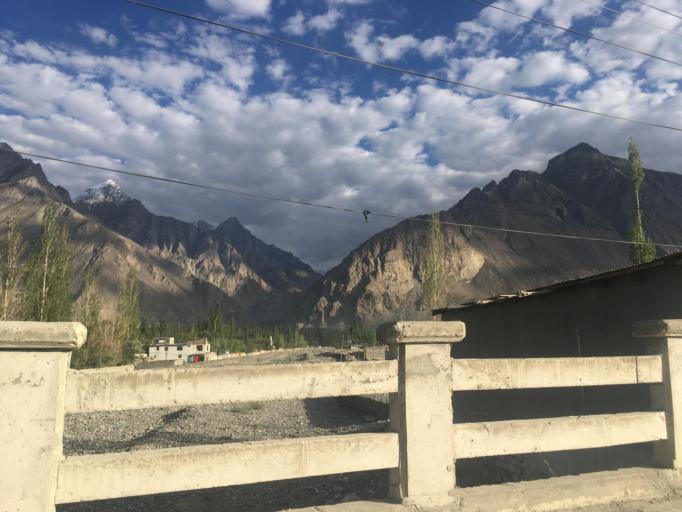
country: PK
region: Gilgit-Baltistan
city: Skardu
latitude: 35.2982
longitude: 75.6264
